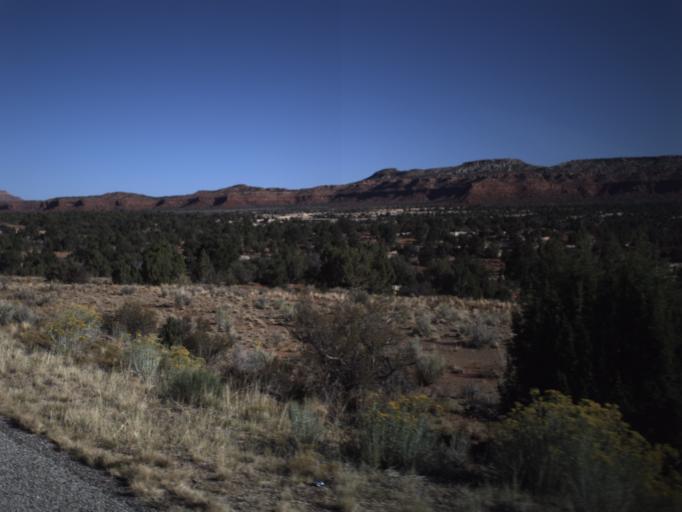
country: US
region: Utah
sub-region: San Juan County
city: Blanding
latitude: 37.6385
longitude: -110.1607
